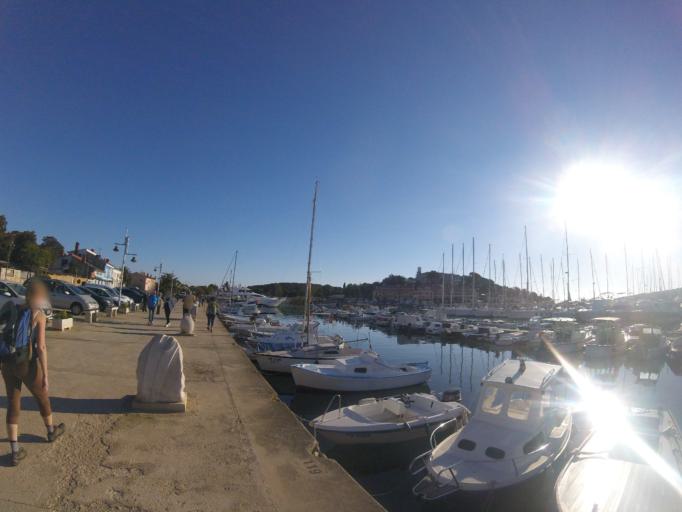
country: HR
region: Istarska
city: Vrsar
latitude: 45.1505
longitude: 13.6024
